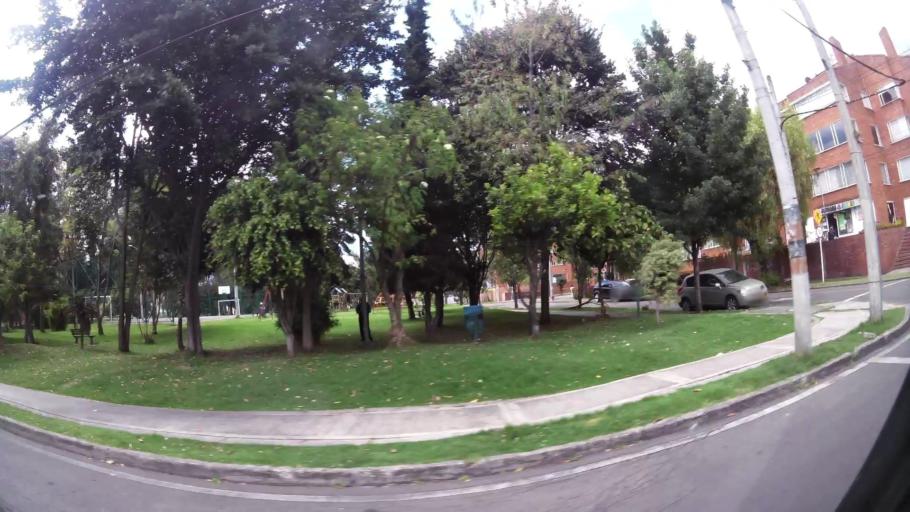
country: CO
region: Bogota D.C.
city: Barrio San Luis
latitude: 4.7055
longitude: -74.0621
